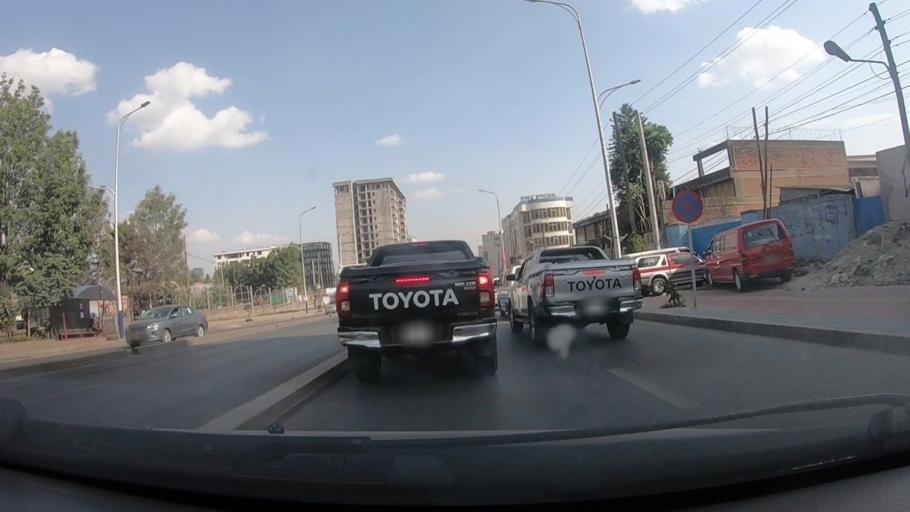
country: ET
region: Adis Abeba
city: Addis Ababa
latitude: 8.9905
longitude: 38.7411
